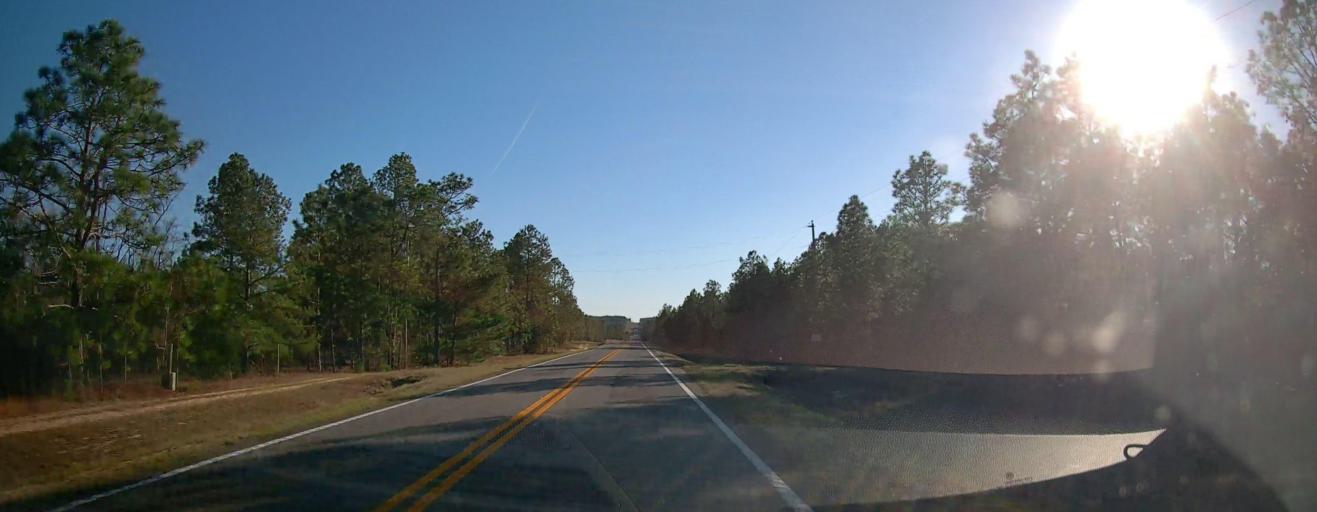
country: US
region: Georgia
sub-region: Taylor County
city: Butler
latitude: 32.5147
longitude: -84.3256
